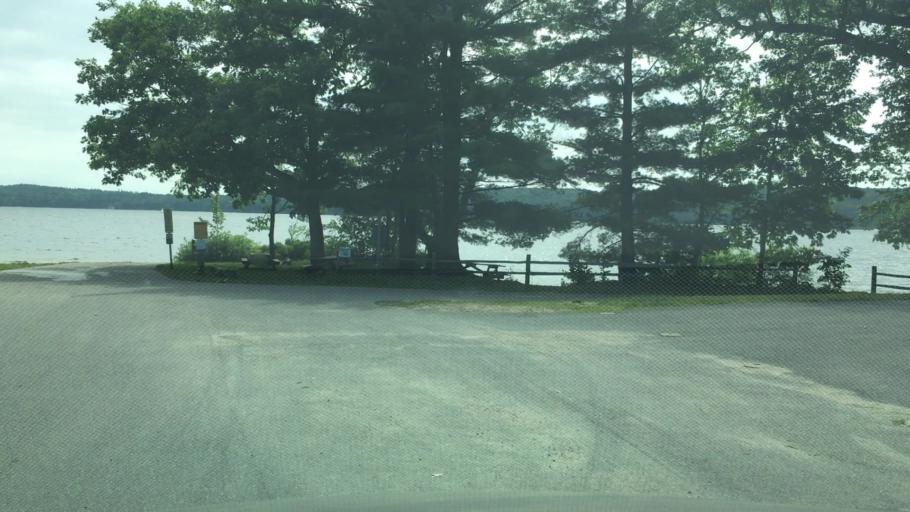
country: US
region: Maine
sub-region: Hancock County
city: Orland
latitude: 44.5850
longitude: -68.6908
